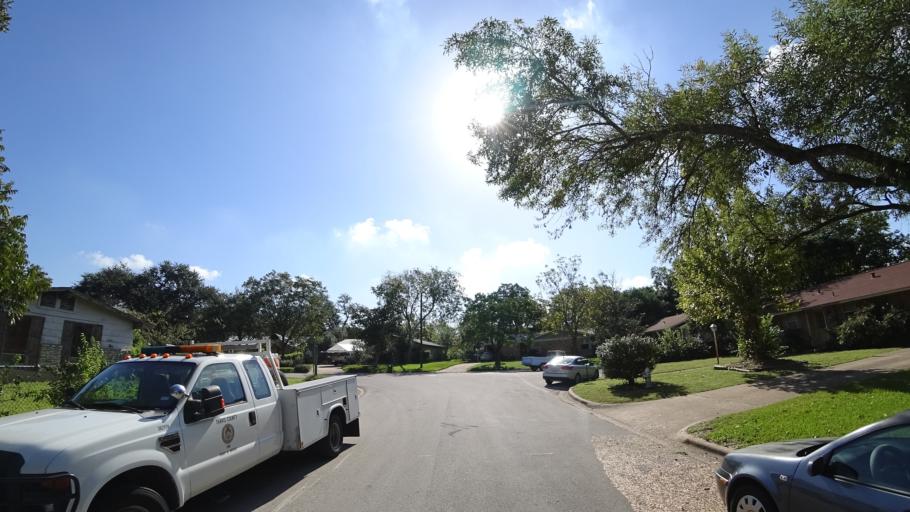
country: US
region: Texas
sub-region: Travis County
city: Austin
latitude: 30.3392
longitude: -97.7089
